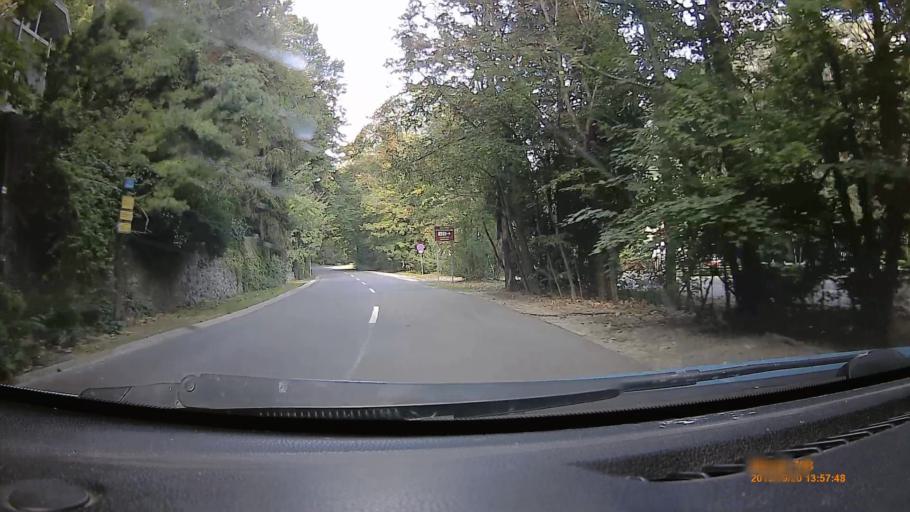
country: HU
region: Borsod-Abauj-Zemplen
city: Sajobabony
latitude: 48.0940
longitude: 20.6192
